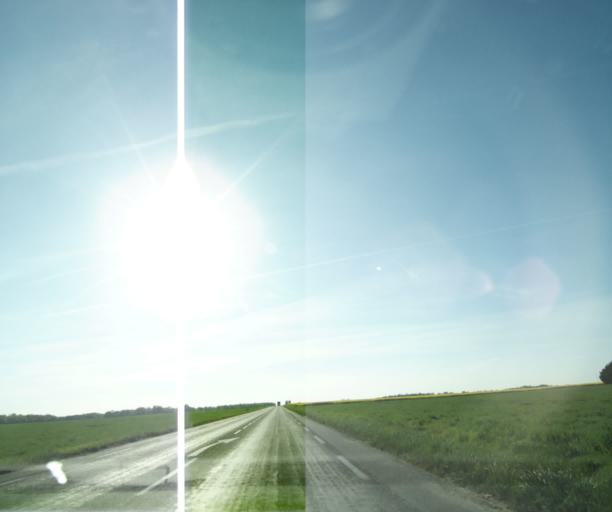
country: FR
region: Ile-de-France
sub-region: Departement de Seine-et-Marne
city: Nangis
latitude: 48.5564
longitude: 2.9911
